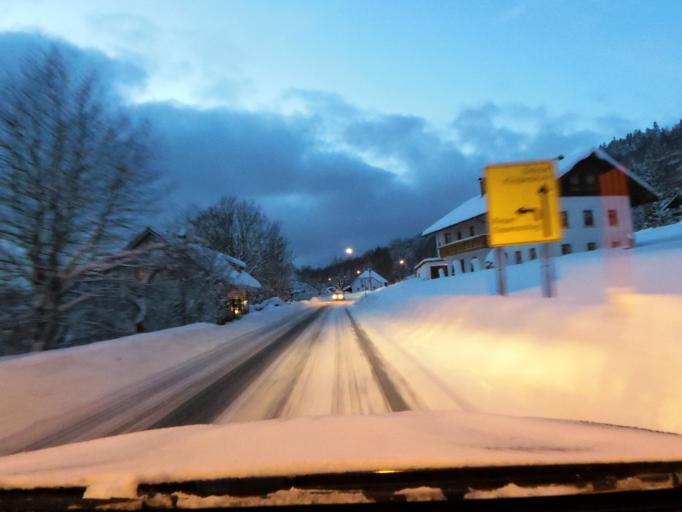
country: DE
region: Bavaria
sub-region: Lower Bavaria
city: Spiegelau
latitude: 48.9121
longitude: 13.3358
